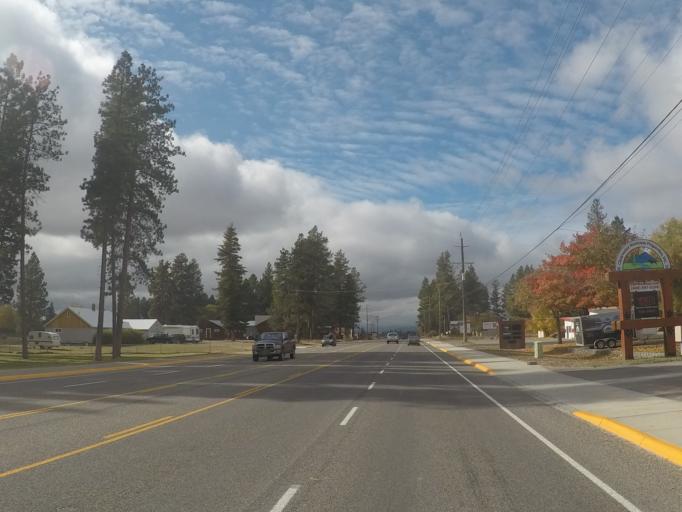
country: US
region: Montana
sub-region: Flathead County
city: Columbia Falls
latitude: 48.3707
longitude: -114.2128
